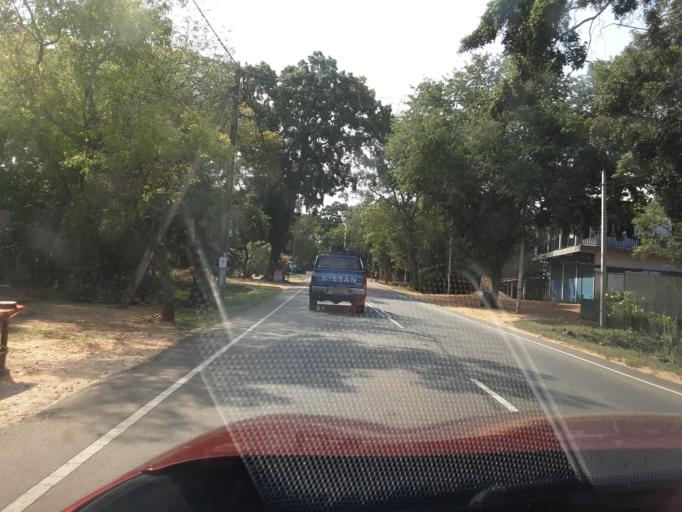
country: LK
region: Uva
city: Haputale
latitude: 6.3550
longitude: 81.1914
